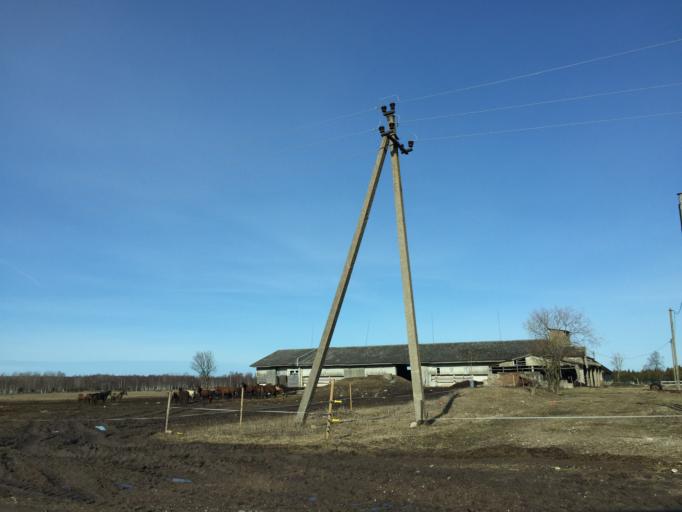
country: EE
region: Laeaene
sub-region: Haapsalu linn
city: Haapsalu
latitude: 58.6732
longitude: 23.5423
